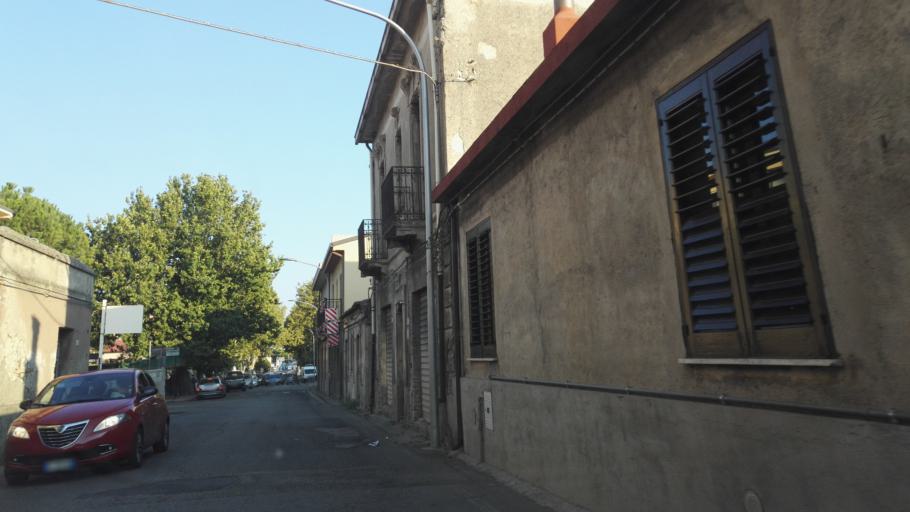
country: IT
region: Calabria
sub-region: Provincia di Reggio Calabria
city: Marina di Gioiosa Ionica
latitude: 38.3015
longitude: 16.3267
